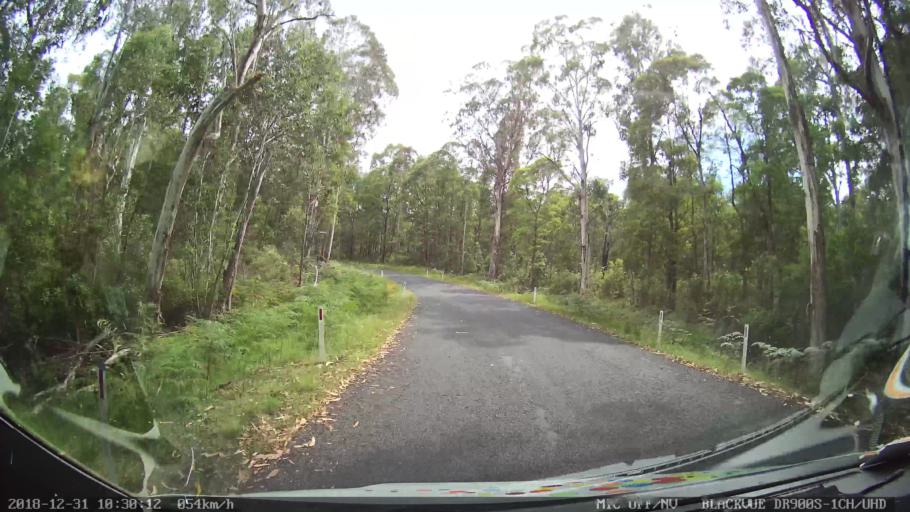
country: AU
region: New South Wales
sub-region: Snowy River
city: Jindabyne
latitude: -36.4650
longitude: 148.1506
